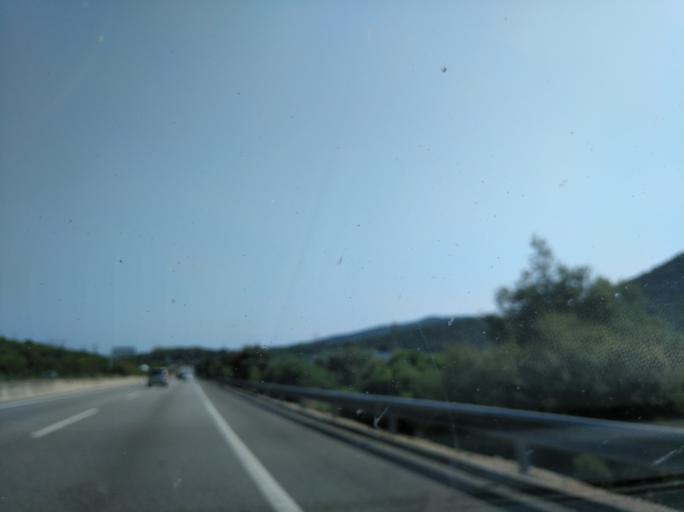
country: ES
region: Catalonia
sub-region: Provincia de Barcelona
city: Argentona
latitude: 41.5694
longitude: 2.3951
